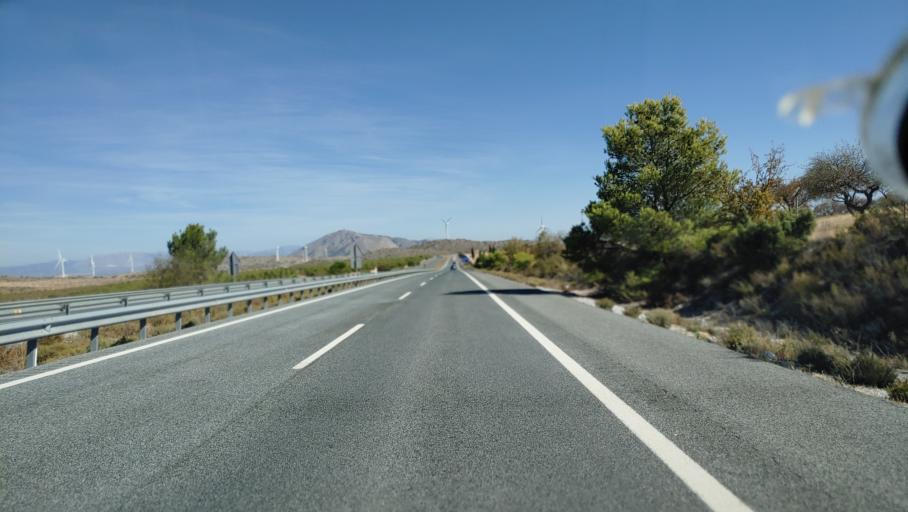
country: ES
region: Andalusia
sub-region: Provincia de Granada
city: Zujar
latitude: 37.4722
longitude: -2.8585
